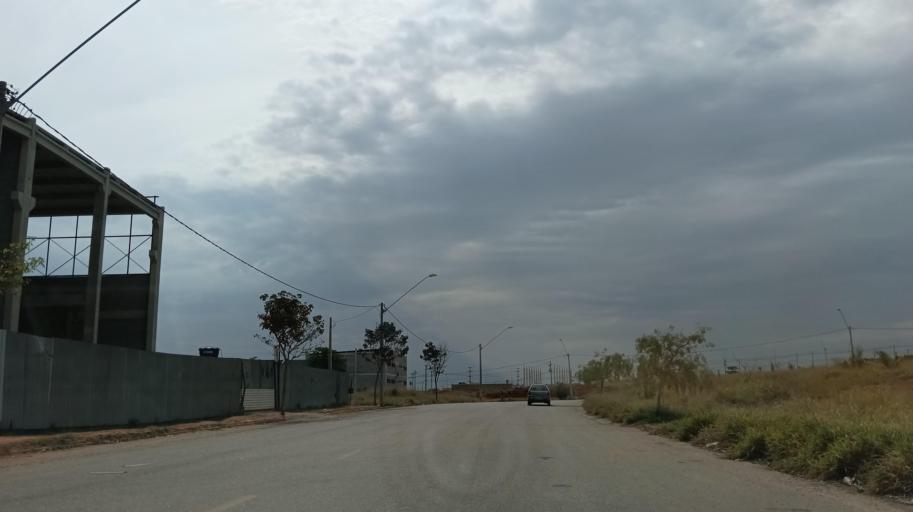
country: BR
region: Sao Paulo
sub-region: Sorocaba
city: Sorocaba
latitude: -23.4560
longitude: -47.4572
